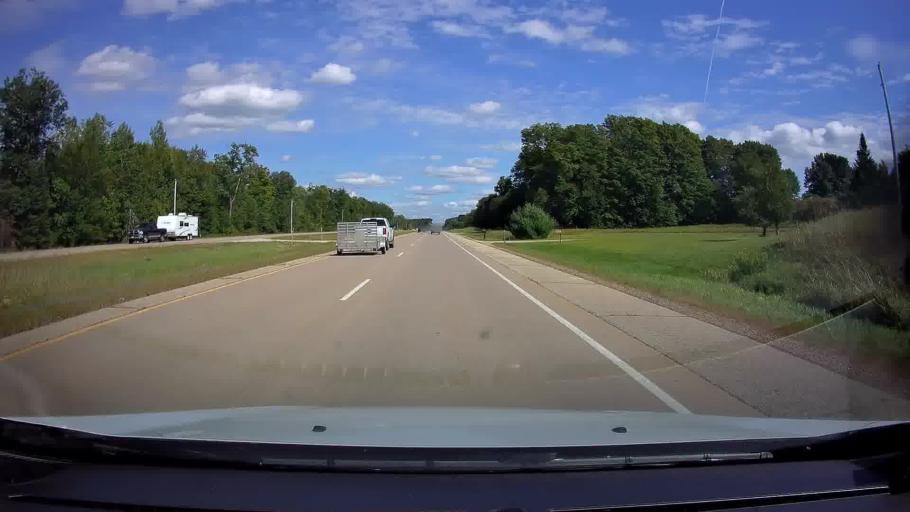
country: US
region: Wisconsin
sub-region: Waupaca County
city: Marion
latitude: 44.7966
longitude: -88.8188
